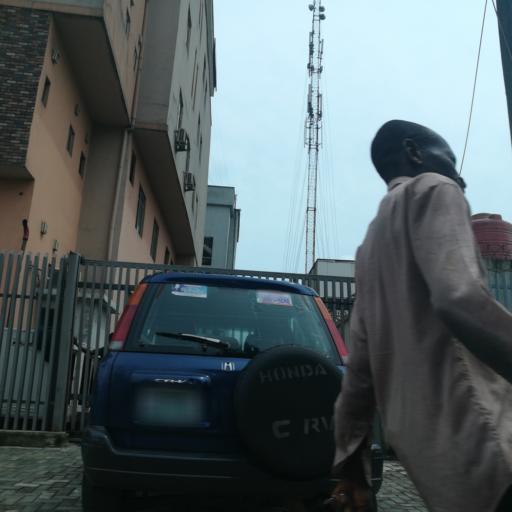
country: NG
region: Rivers
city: Port Harcourt
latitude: 4.8048
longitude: 7.0074
